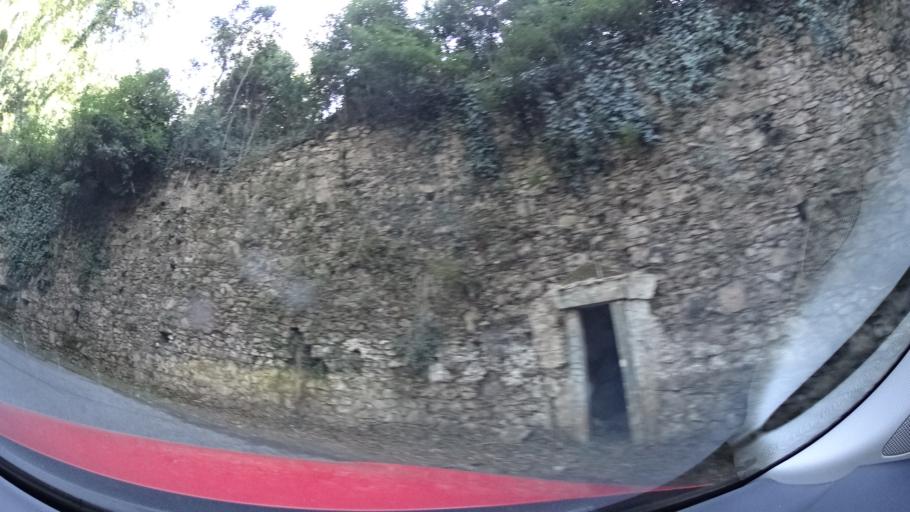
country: PT
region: Lisbon
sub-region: Sintra
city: Sintra
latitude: 38.7915
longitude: -9.3990
